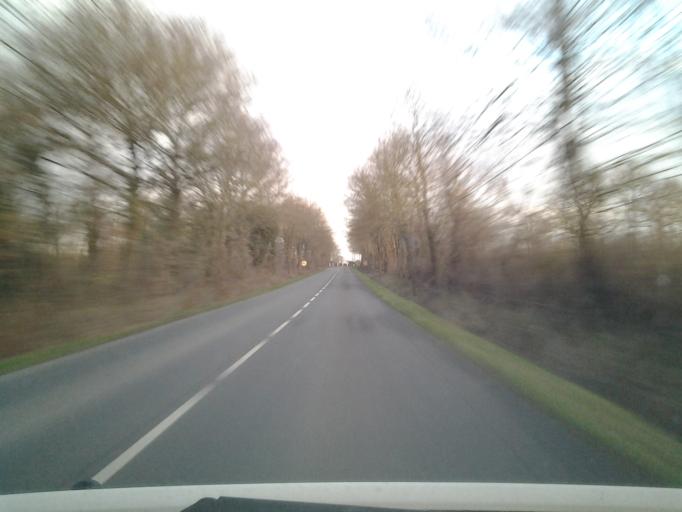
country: FR
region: Pays de la Loire
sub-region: Departement de la Vendee
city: Les Clouzeaux
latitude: 46.6364
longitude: -1.4802
